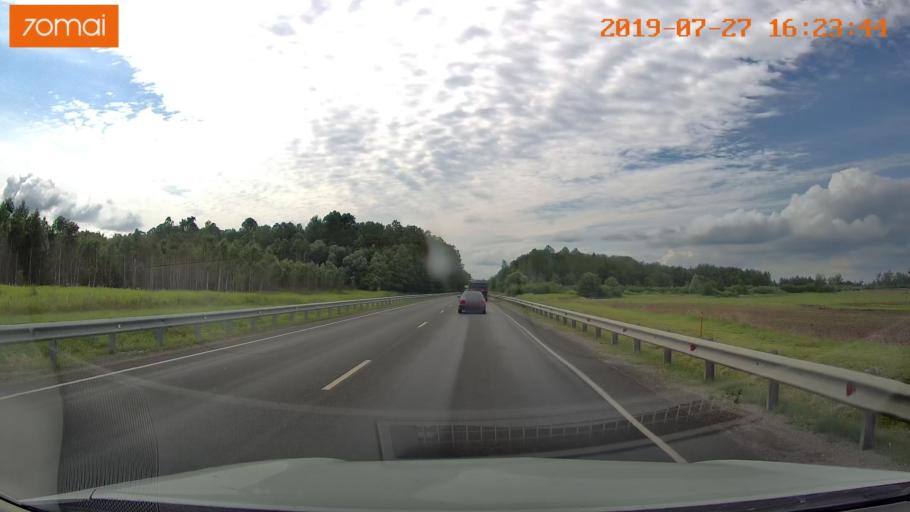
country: RU
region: Kaliningrad
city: Zheleznodorozhnyy
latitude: 54.6319
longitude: 21.4675
